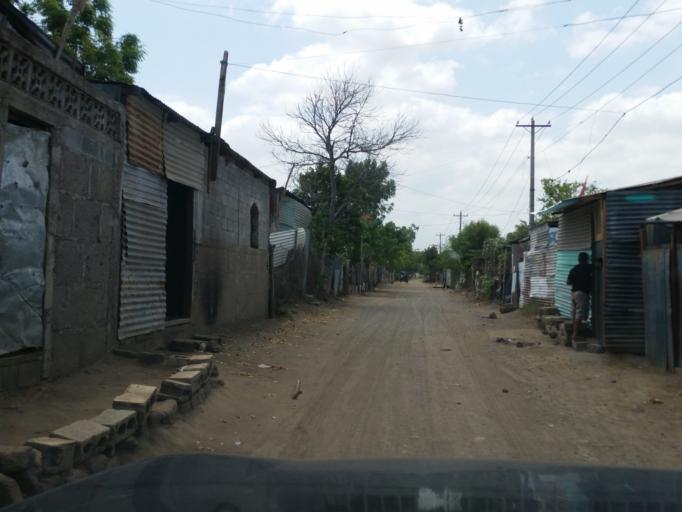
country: NI
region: Managua
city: Managua
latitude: 12.1453
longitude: -86.1908
